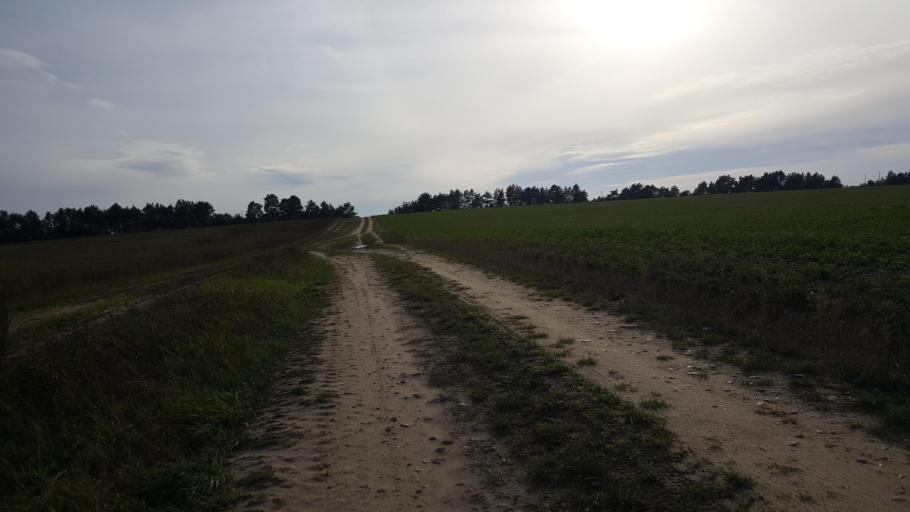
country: BY
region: Brest
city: Kamyanyets
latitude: 52.4010
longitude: 23.8576
